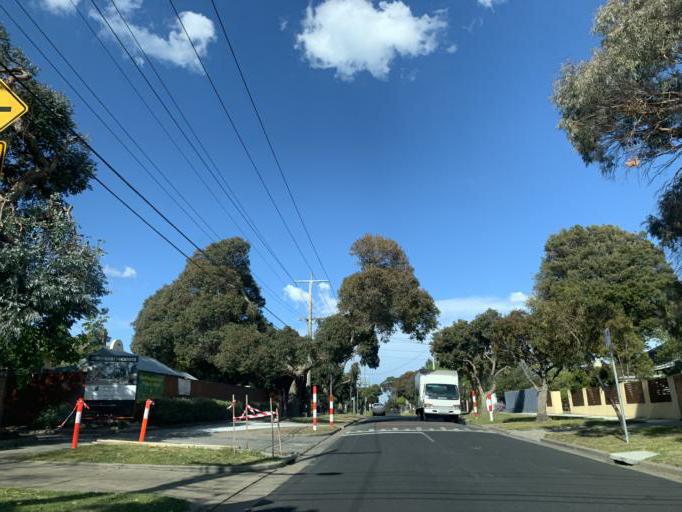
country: AU
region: Victoria
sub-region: Bayside
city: Black Rock
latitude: -37.9568
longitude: 145.0217
